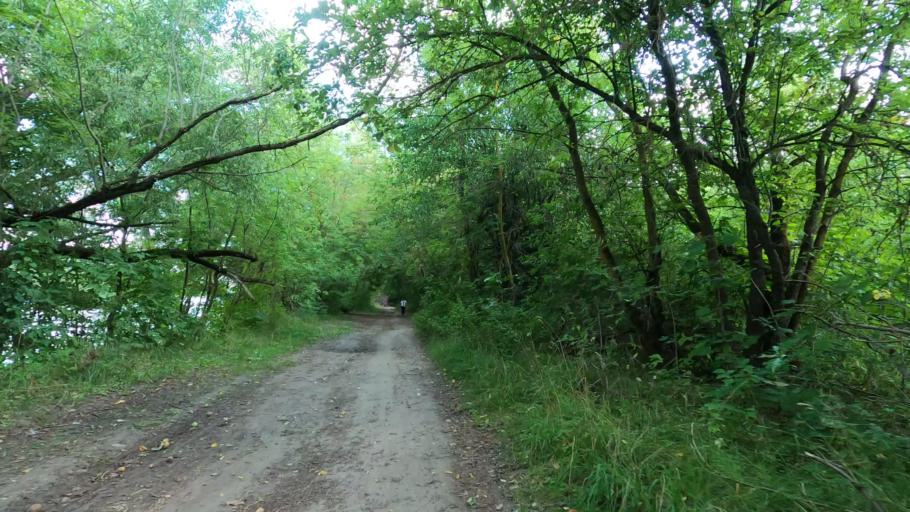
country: RU
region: Moskovskaya
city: Peski
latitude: 55.2029
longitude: 38.7443
